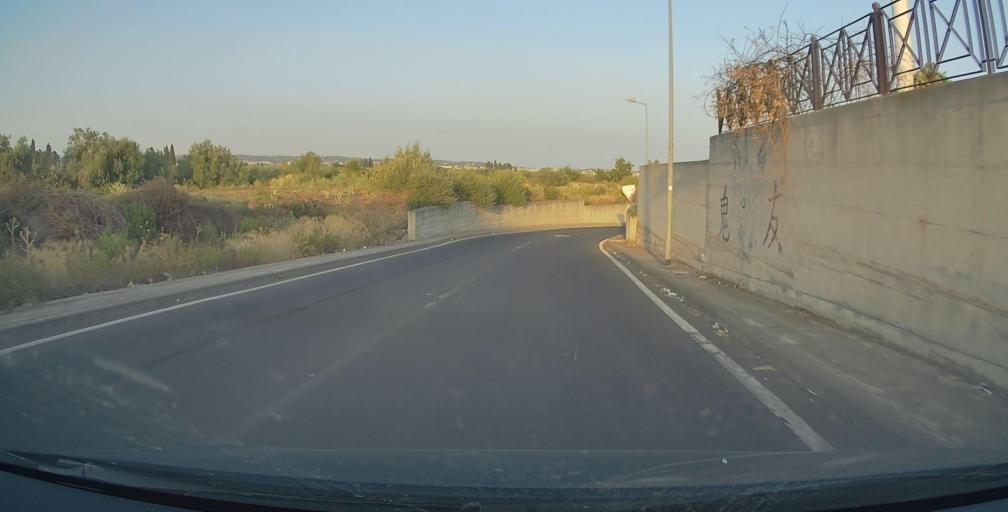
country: IT
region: Sicily
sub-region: Catania
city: Palazzolo
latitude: 37.5496
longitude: 14.9470
